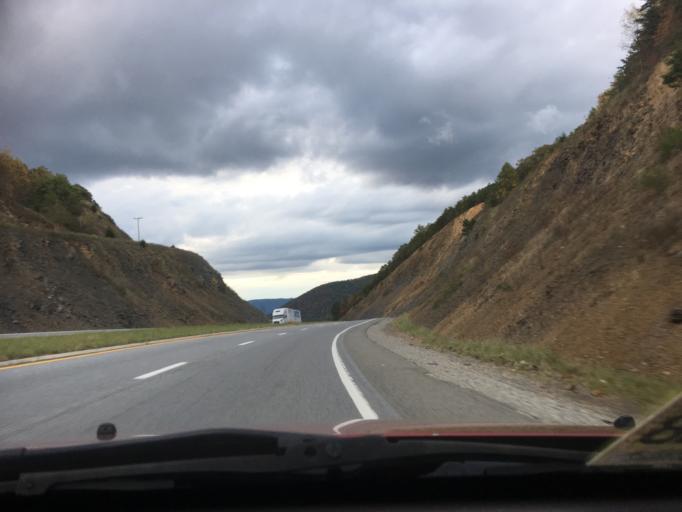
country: US
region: Virginia
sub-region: Pulaski County
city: Dublin
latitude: 37.1801
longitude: -80.7195
